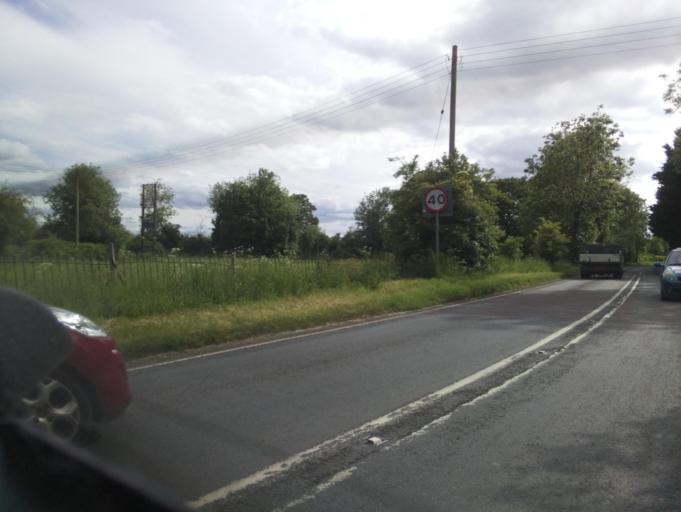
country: GB
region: England
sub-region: Worcestershire
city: South Littleton
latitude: 52.0951
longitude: -1.8727
